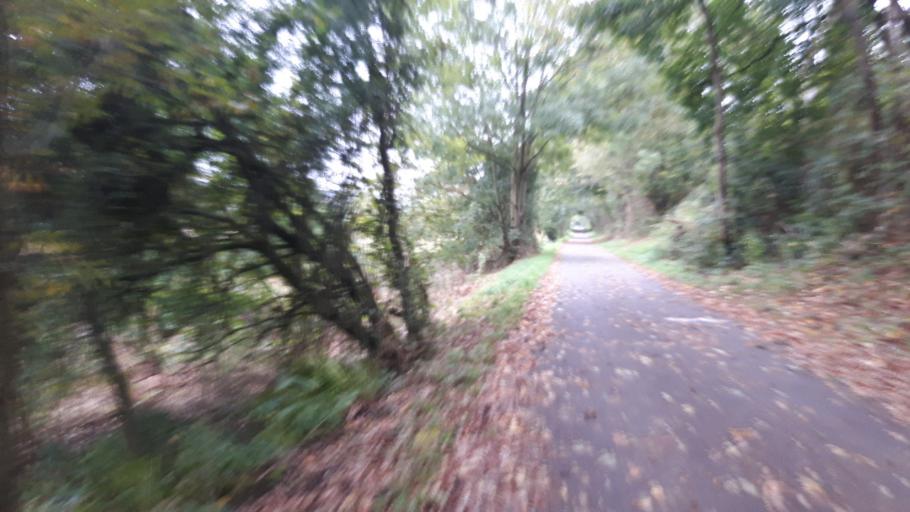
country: DE
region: North Rhine-Westphalia
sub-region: Regierungsbezirk Koln
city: Hennef
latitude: 50.7710
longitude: 7.3307
